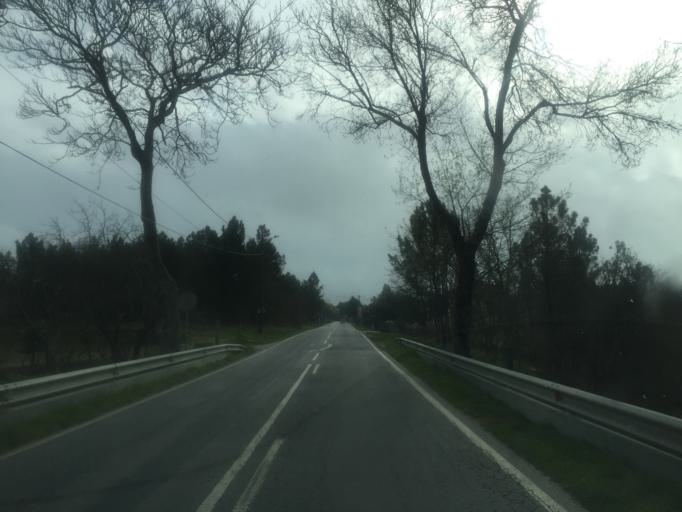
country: PT
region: Guarda
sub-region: Seia
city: Seia
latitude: 40.3976
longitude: -7.7417
